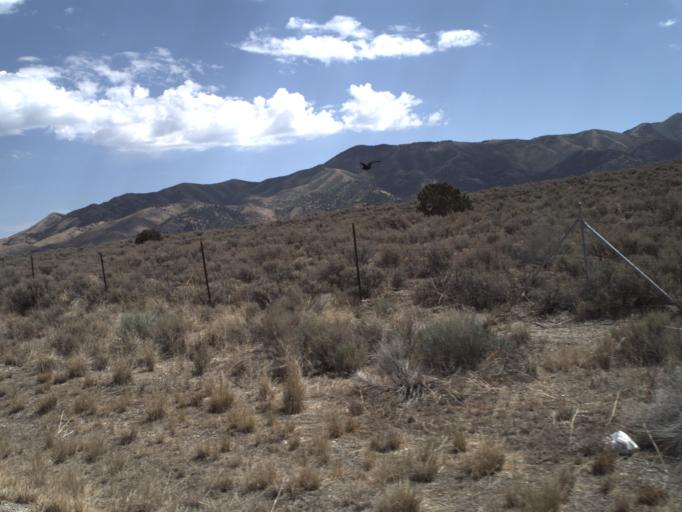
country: US
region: Utah
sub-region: Tooele County
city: Tooele
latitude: 40.4248
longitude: -112.3808
